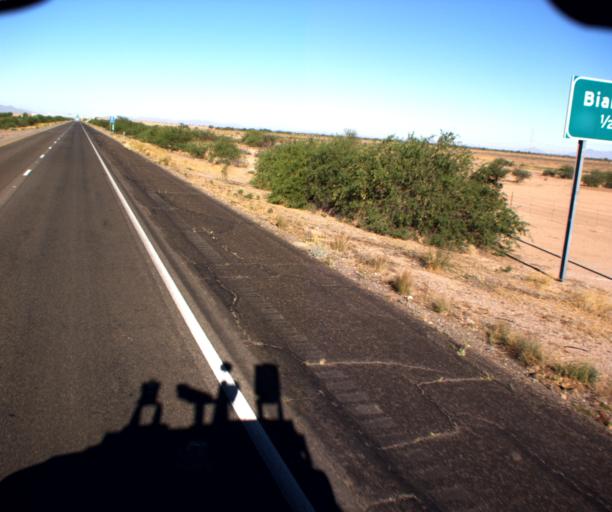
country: US
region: Arizona
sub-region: Pinal County
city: Casa Grande
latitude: 32.8282
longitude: -111.8164
